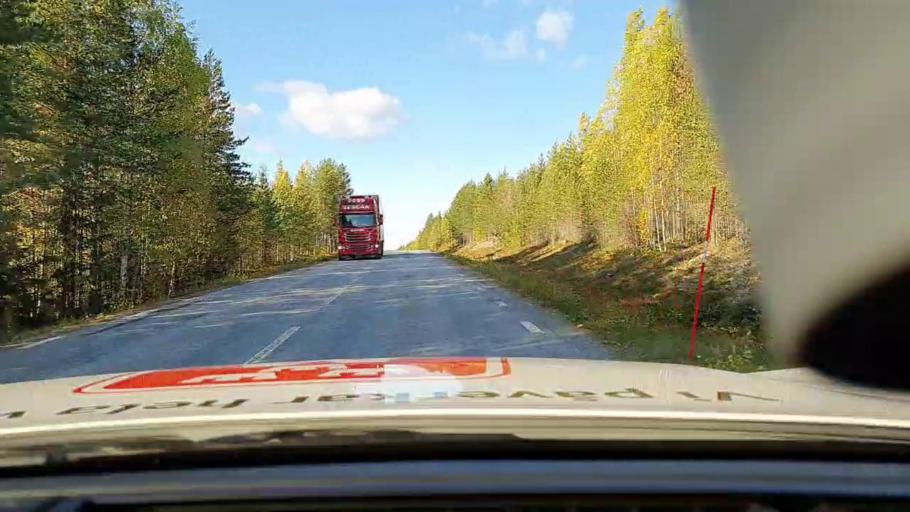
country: SE
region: Norrbotten
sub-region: Pitea Kommun
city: Norrfjarden
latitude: 65.4522
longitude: 21.4566
